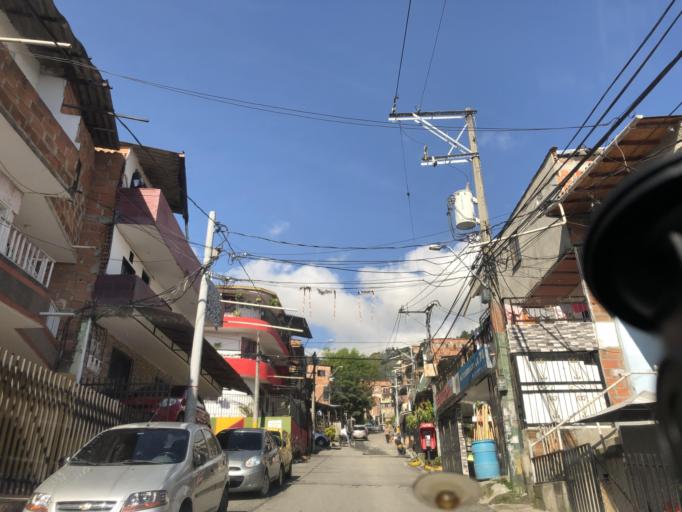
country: CO
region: Antioquia
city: Bello
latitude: 6.3151
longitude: -75.5795
